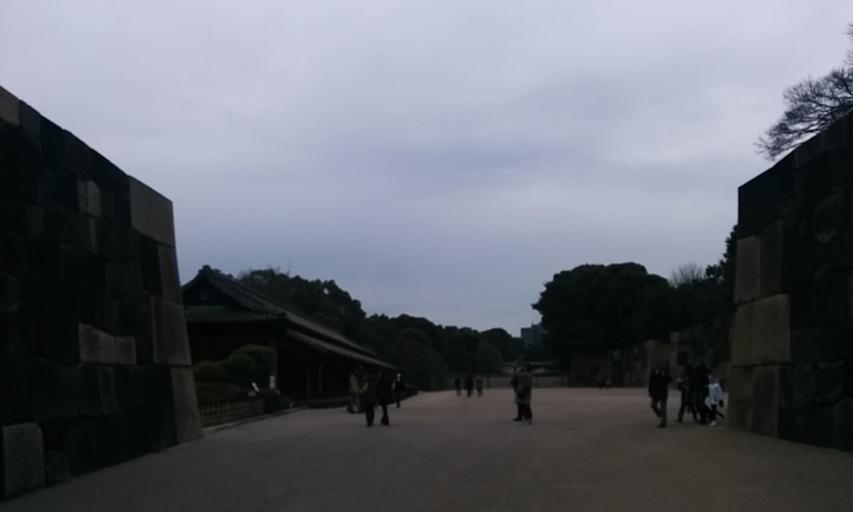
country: JP
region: Tokyo
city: Tokyo
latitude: 35.6862
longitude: 139.7580
